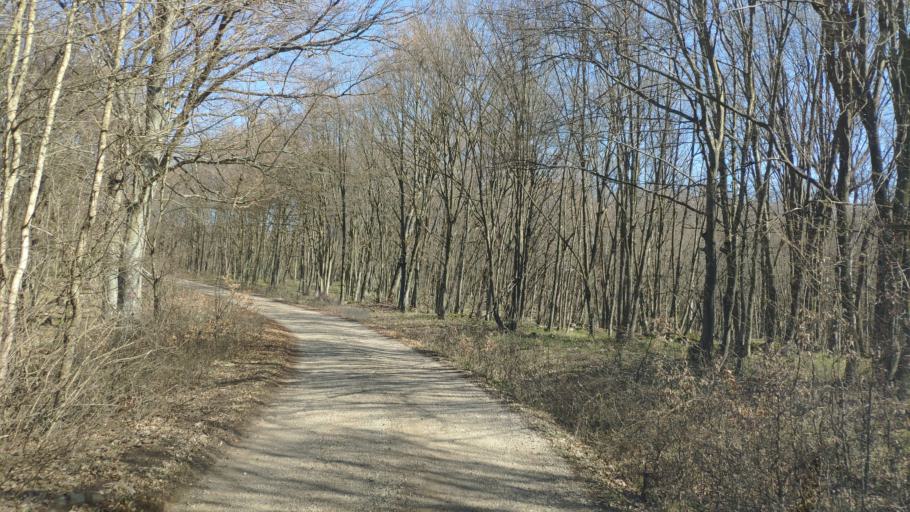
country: SK
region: Kosicky
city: Roznava
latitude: 48.5950
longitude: 20.4111
